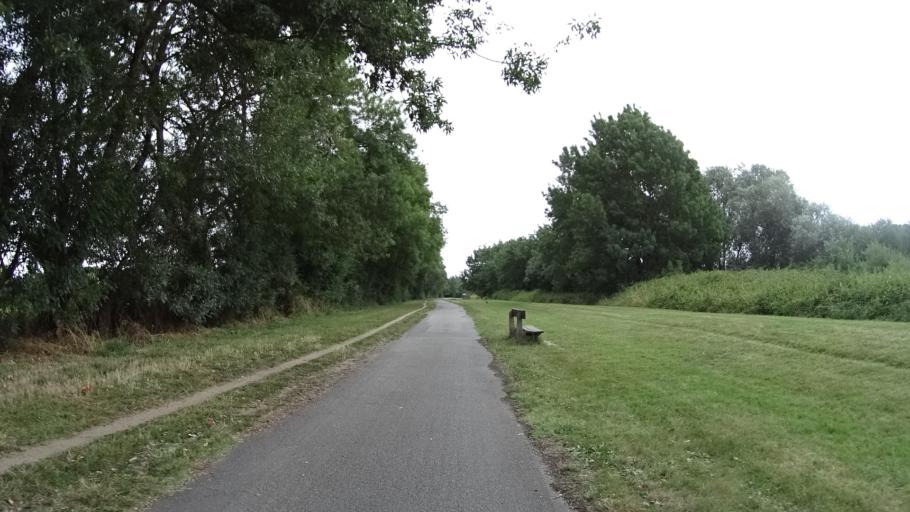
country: FR
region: Pays de la Loire
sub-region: Departement de la Loire-Atlantique
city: Thouare-sur-Loire
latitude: 47.2557
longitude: -1.4443
